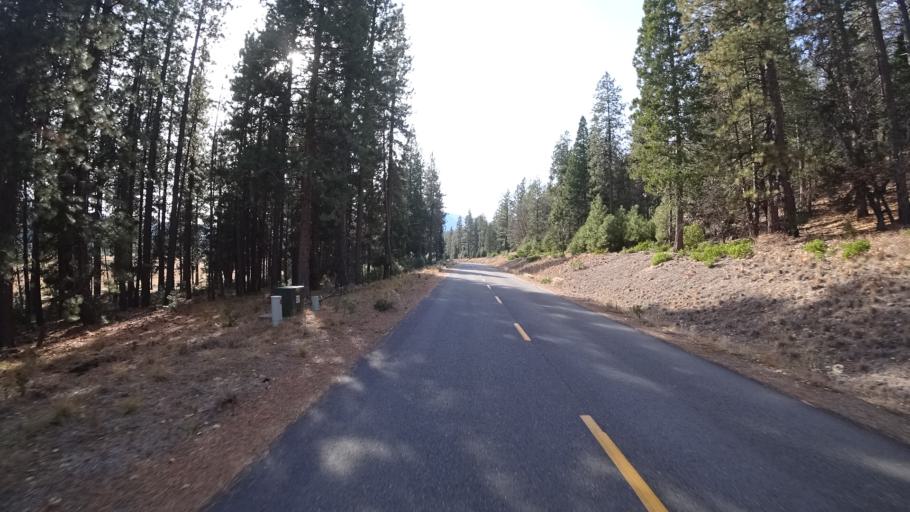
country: US
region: California
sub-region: Siskiyou County
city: Weed
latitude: 41.4030
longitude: -122.3856
